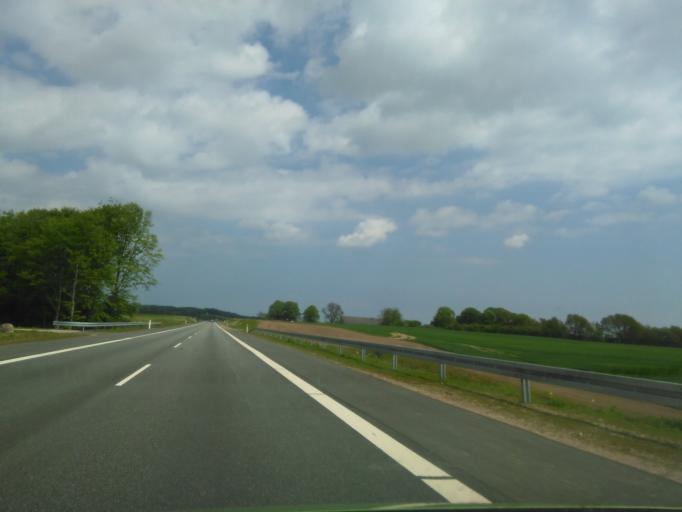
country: DK
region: Central Jutland
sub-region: Odder Kommune
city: Odder
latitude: 55.9807
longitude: 10.0924
